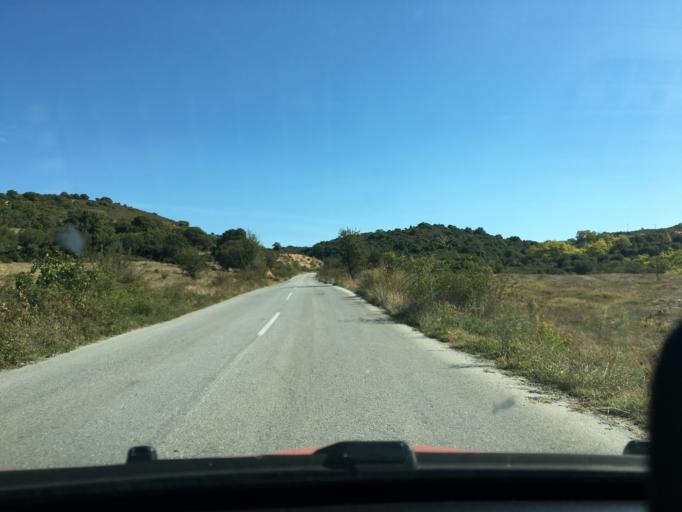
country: GR
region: Central Macedonia
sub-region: Nomos Chalkidikis
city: Megali Panagia
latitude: 40.3854
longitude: 23.7164
